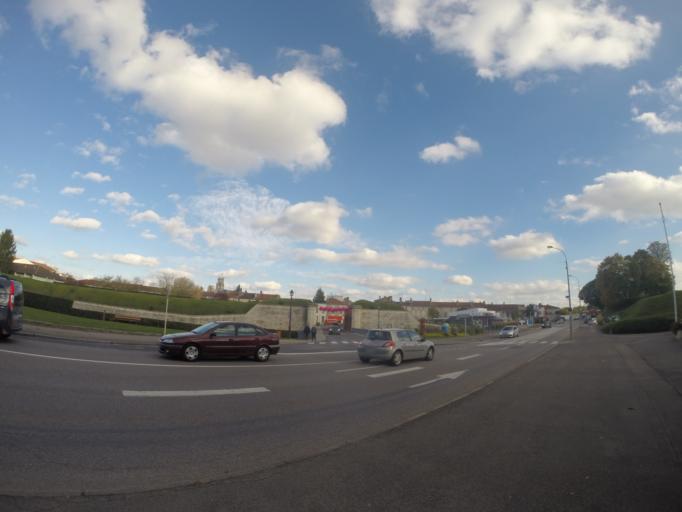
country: FR
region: Lorraine
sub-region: Departement de Meurthe-et-Moselle
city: Toul
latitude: 48.6744
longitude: 5.8852
